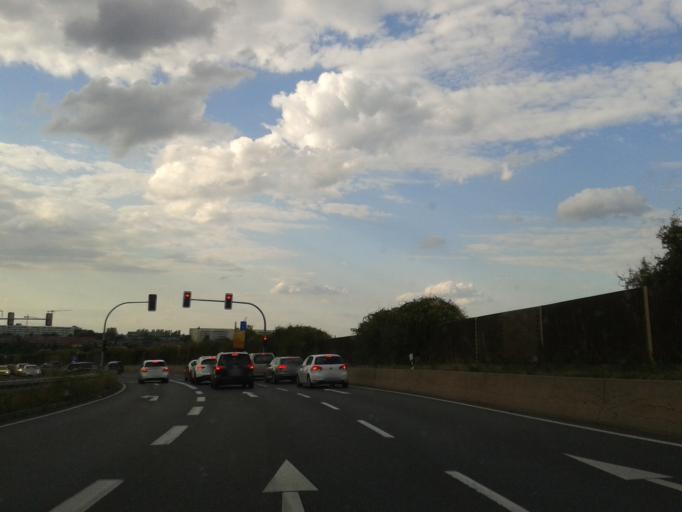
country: DE
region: Saxony
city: Bannewitz
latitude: 51.0094
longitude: 13.7302
